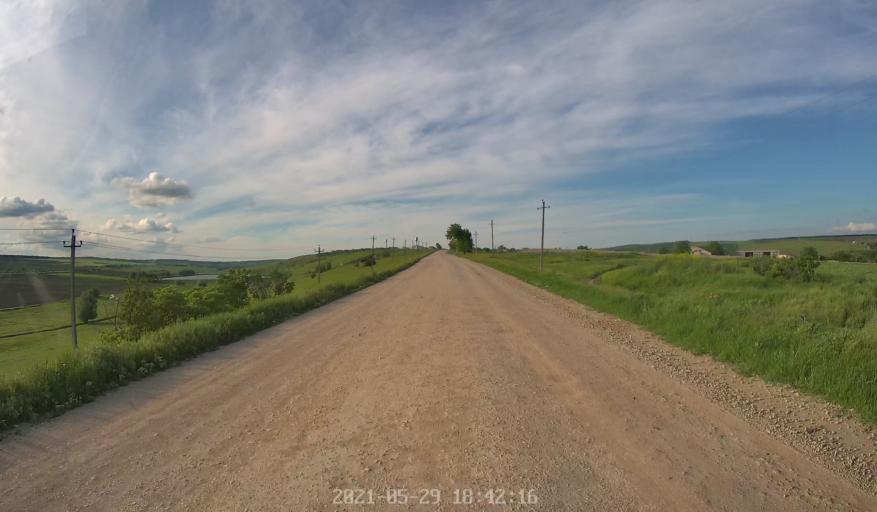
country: MD
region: Chisinau
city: Singera
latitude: 46.8110
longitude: 28.9616
